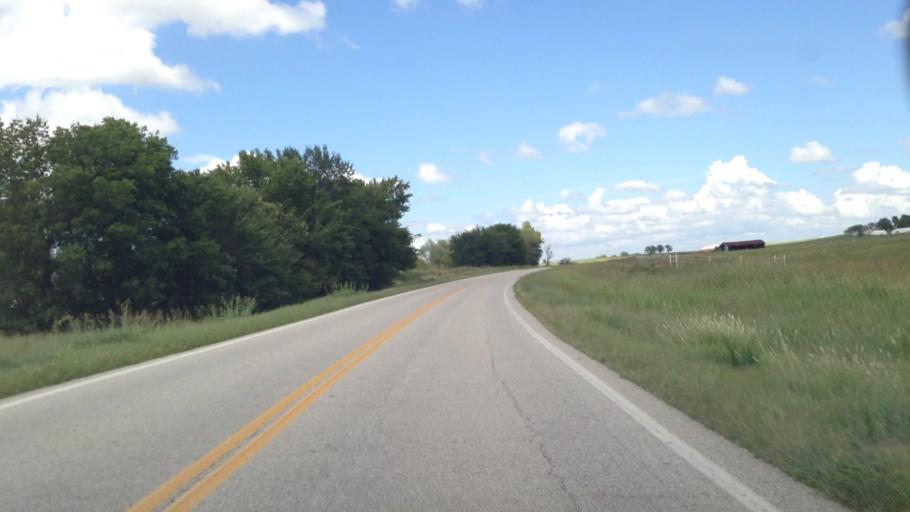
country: US
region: Oklahoma
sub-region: Craig County
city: Vinita
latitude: 36.8209
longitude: -95.1427
